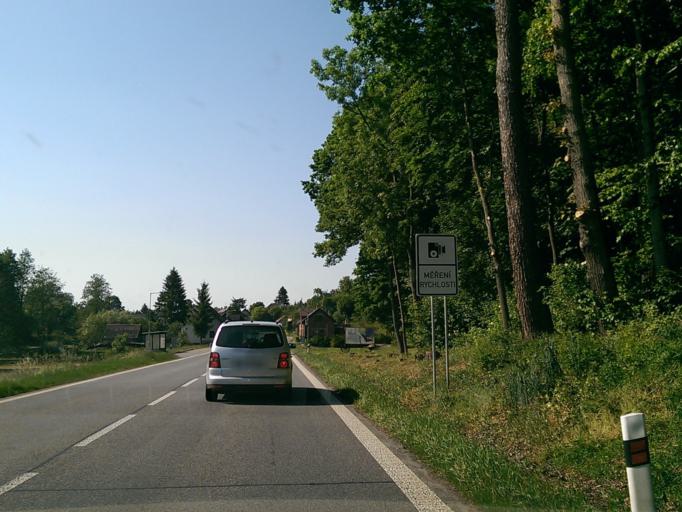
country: CZ
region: Liberecky
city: Rovensko pod Troskami
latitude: 50.5173
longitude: 15.2506
